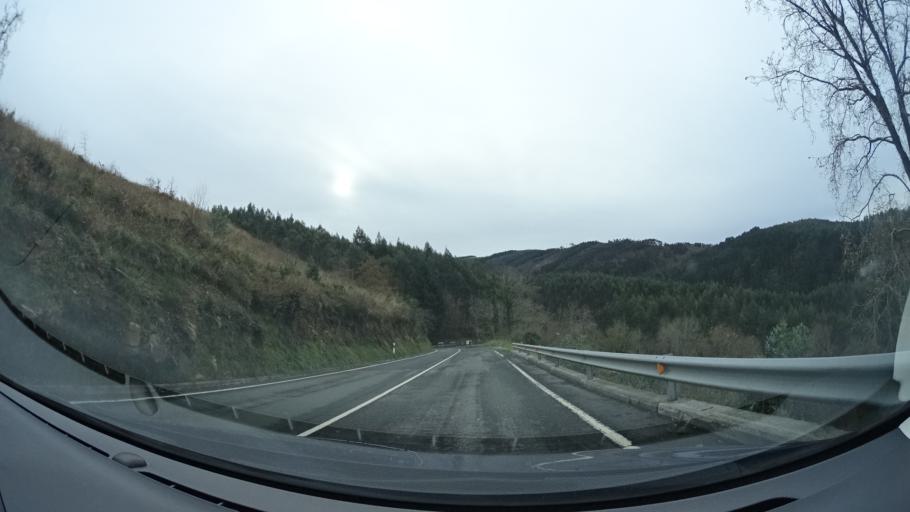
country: ES
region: Basque Country
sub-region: Bizkaia
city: Bakio
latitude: 43.3874
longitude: -2.7711
